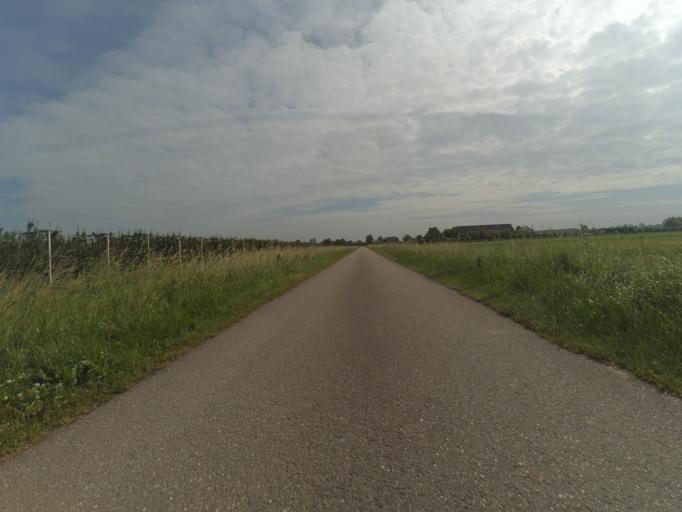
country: NL
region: Utrecht
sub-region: Gemeente Wijk bij Duurstede
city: Wijk bij Duurstede
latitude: 51.9458
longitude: 5.3452
